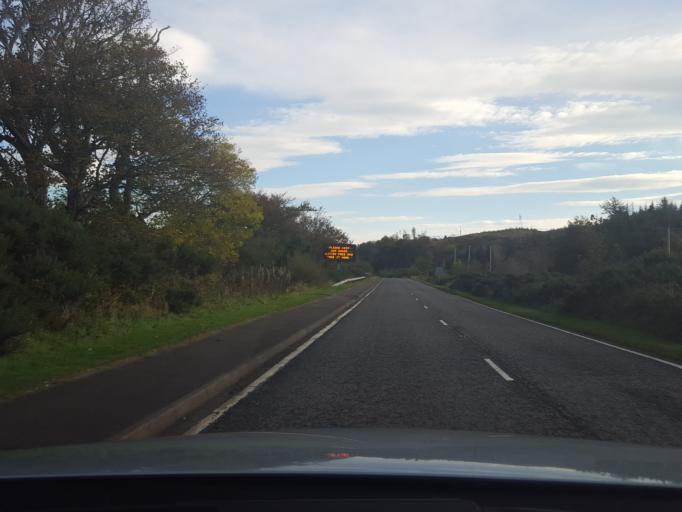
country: GB
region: Scotland
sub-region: Highland
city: Portree
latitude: 57.2823
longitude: -5.6225
